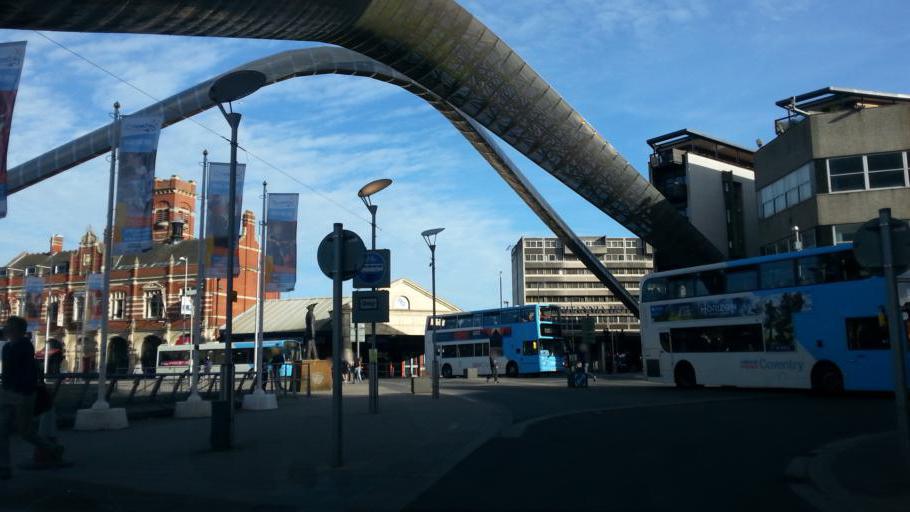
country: GB
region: England
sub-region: Coventry
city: Coventry
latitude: 52.4105
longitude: -1.5092
